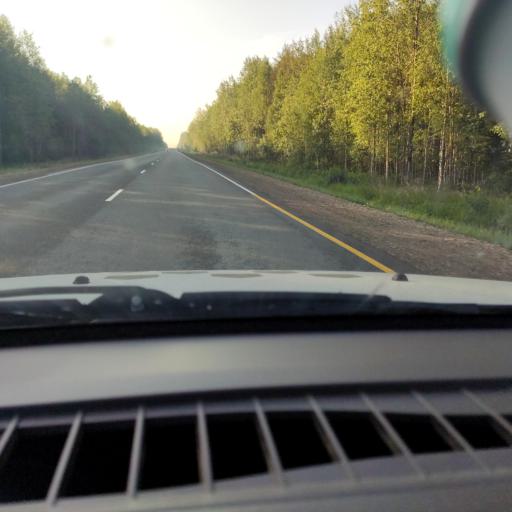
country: RU
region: Kirov
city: Chernaya Kholunitsa
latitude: 58.8055
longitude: 51.8491
